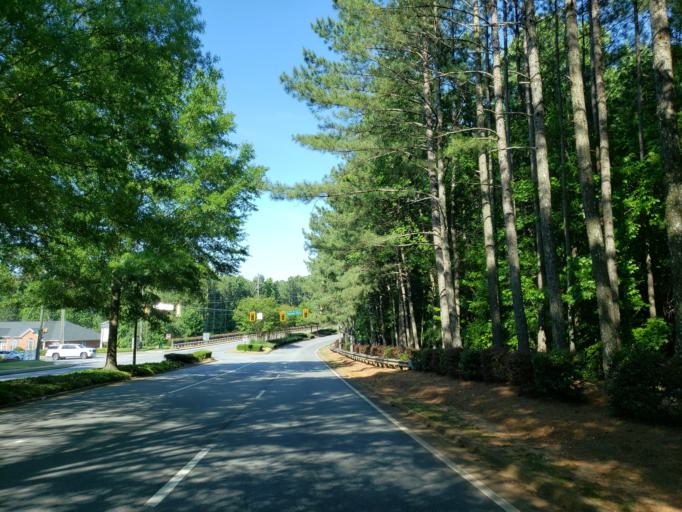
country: US
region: Georgia
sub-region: Cherokee County
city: Woodstock
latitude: 34.1288
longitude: -84.5775
